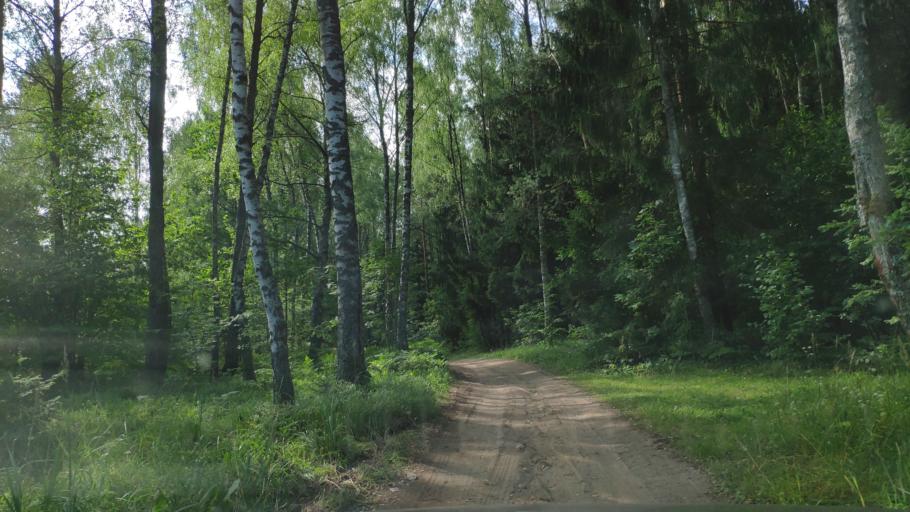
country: BY
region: Minsk
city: Zaslawye
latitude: 53.9671
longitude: 27.2965
